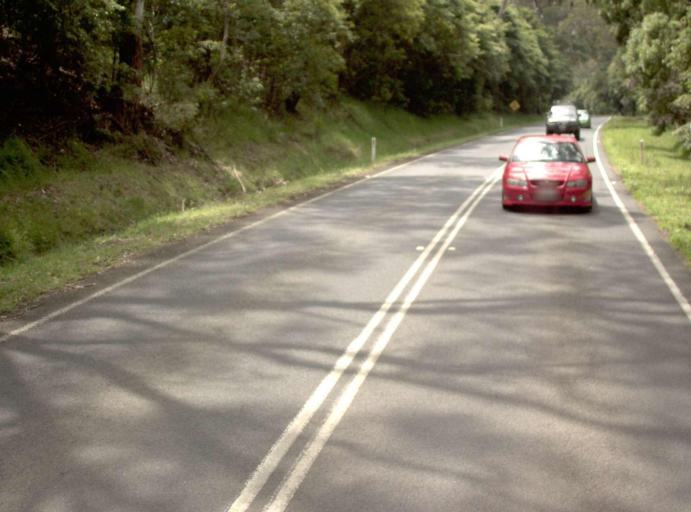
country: AU
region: Victoria
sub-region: Latrobe
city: Traralgon
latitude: -38.4331
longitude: 146.7348
